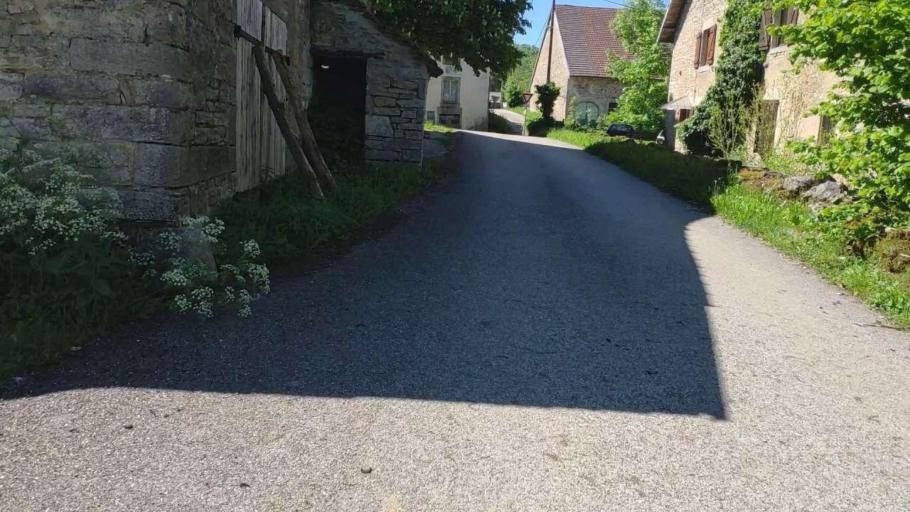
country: FR
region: Franche-Comte
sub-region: Departement du Jura
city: Clairvaux-les-Lacs
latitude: 46.6970
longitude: 5.7249
